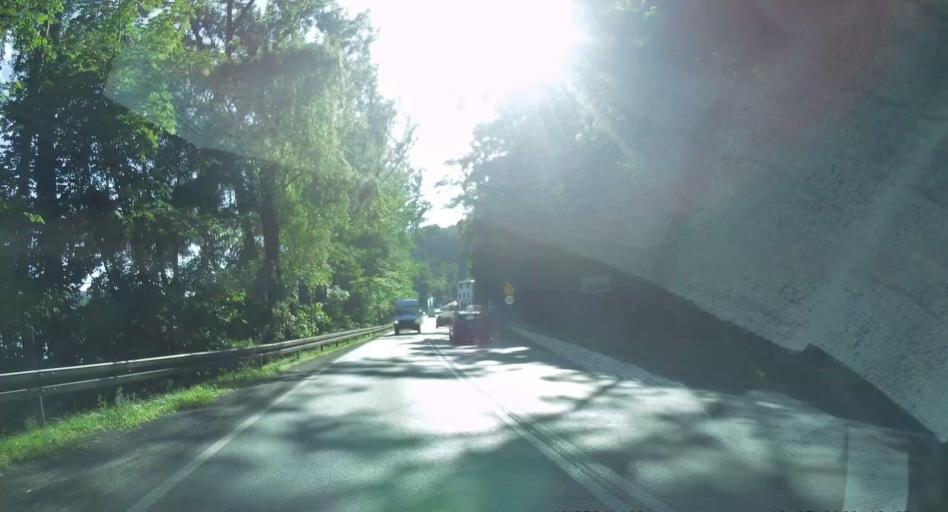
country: PL
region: Lesser Poland Voivodeship
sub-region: Powiat brzeski
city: Czchow
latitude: 49.8111
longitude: 20.6775
